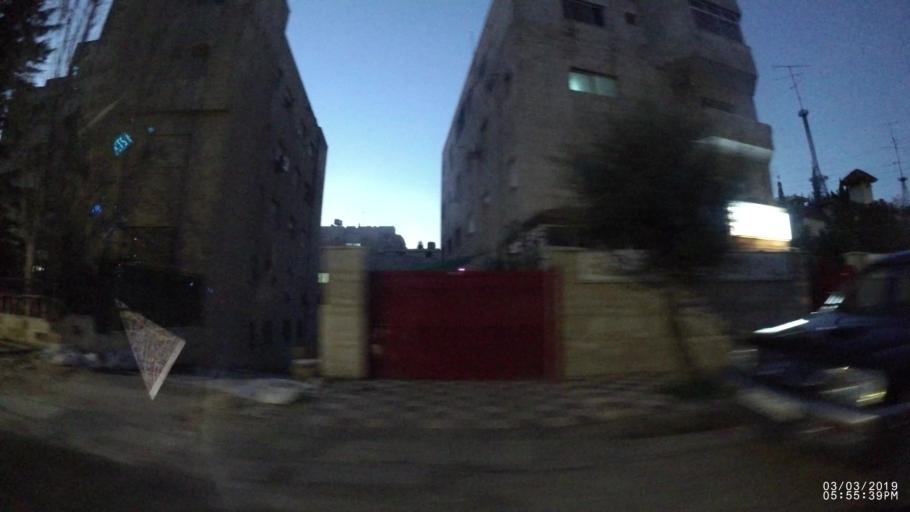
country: JO
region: Amman
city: Al Jubayhah
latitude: 31.9806
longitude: 35.8815
